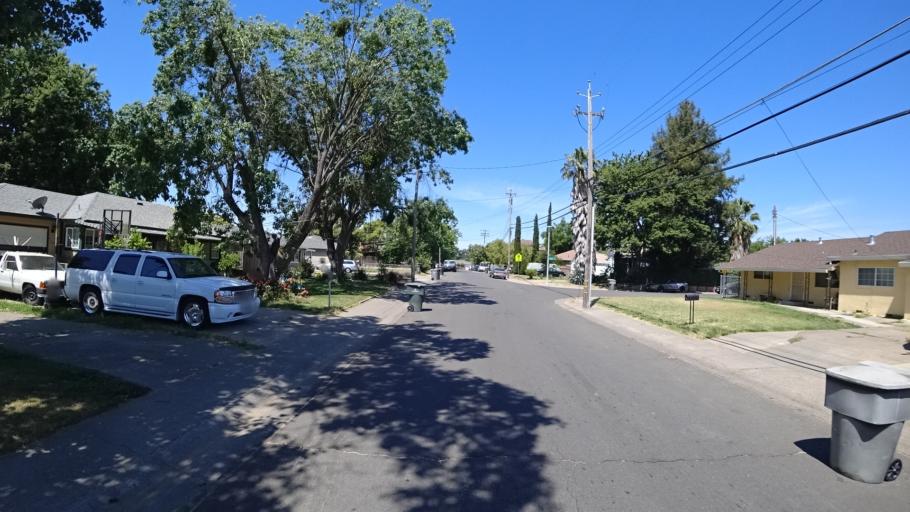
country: US
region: California
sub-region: Sacramento County
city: Florin
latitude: 38.5341
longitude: -121.4170
